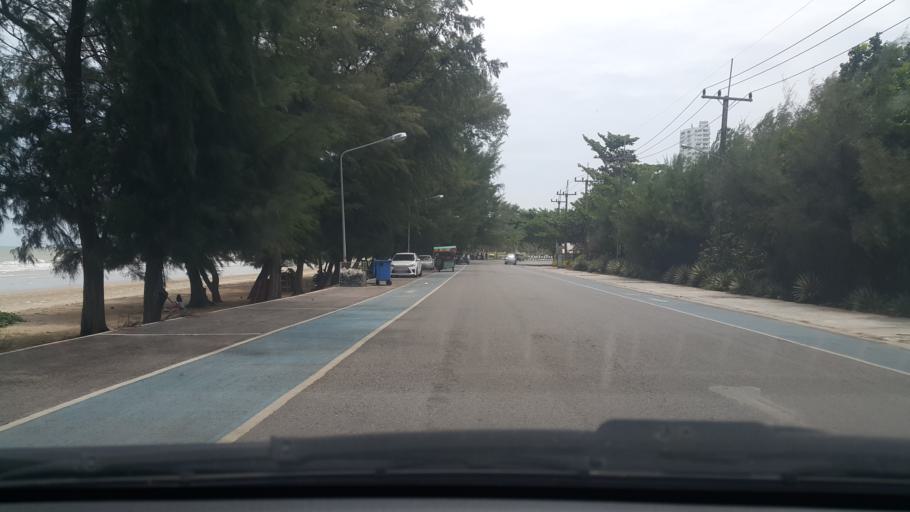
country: TH
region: Rayong
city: Rayong
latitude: 12.6097
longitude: 101.3874
